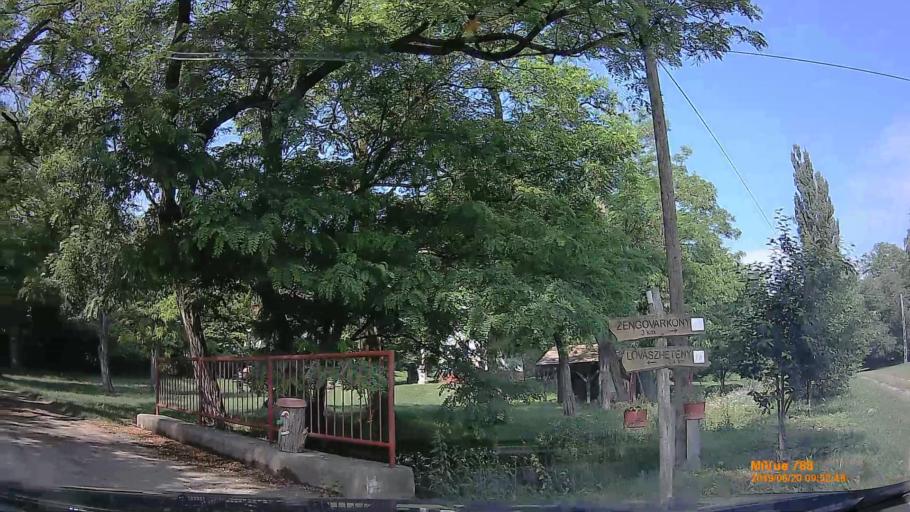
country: HU
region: Baranya
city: Pecsvarad
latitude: 46.1740
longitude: 18.4680
